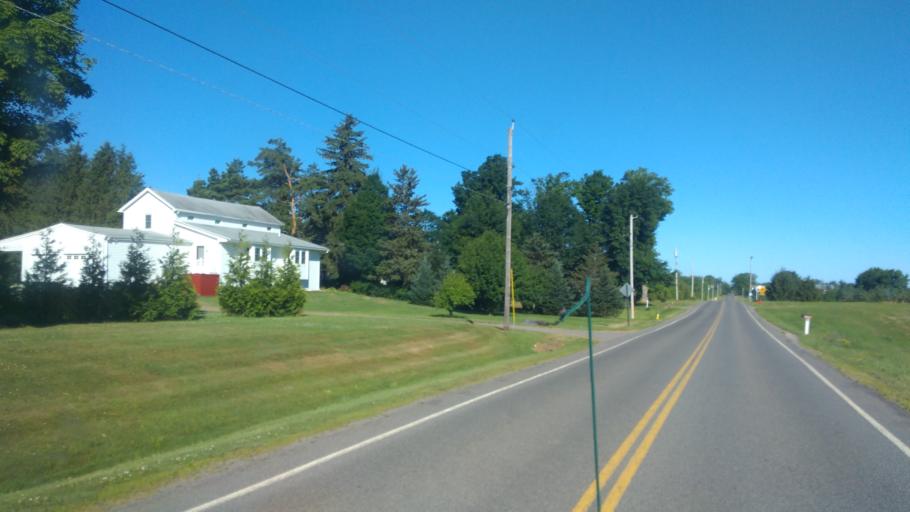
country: US
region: New York
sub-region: Wayne County
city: Sodus
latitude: 43.2762
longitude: -77.1159
